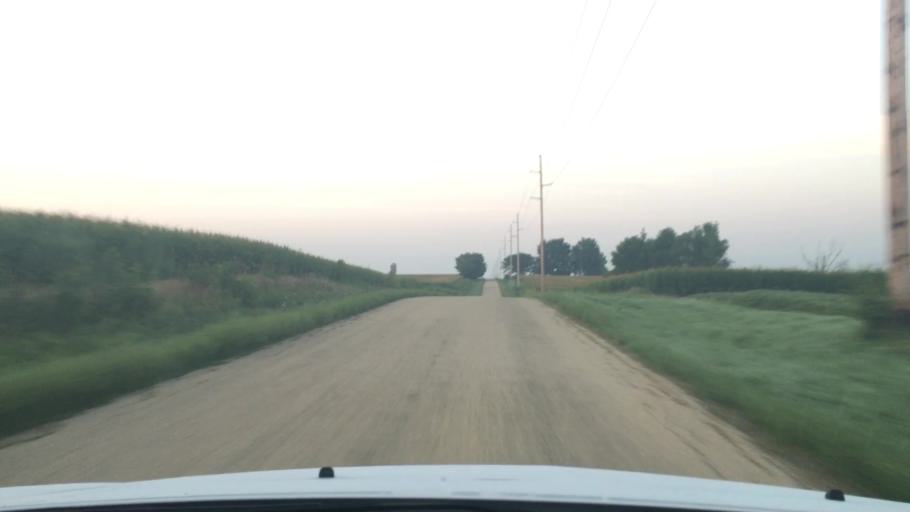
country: US
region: Illinois
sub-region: Ogle County
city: Rochelle
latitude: 41.8664
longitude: -89.0008
